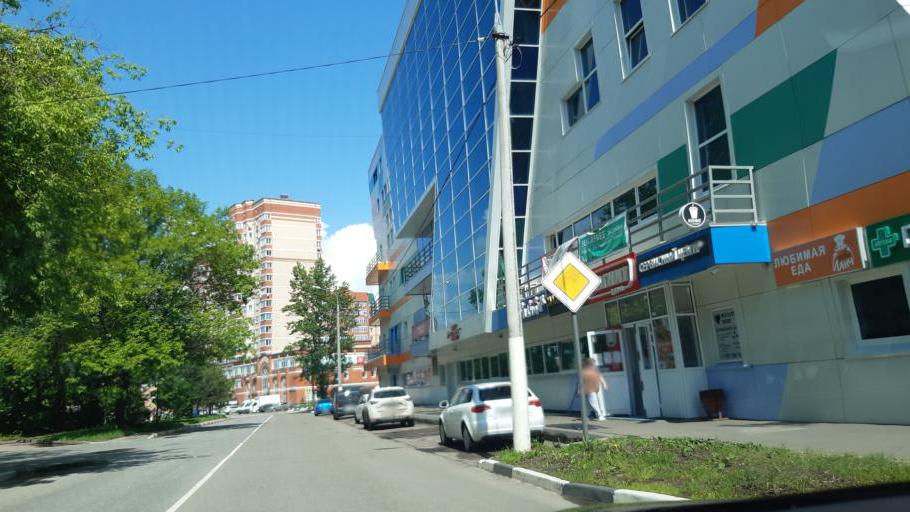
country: RU
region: Moskovskaya
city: Dolgoprudnyy
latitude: 55.9456
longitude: 37.4990
